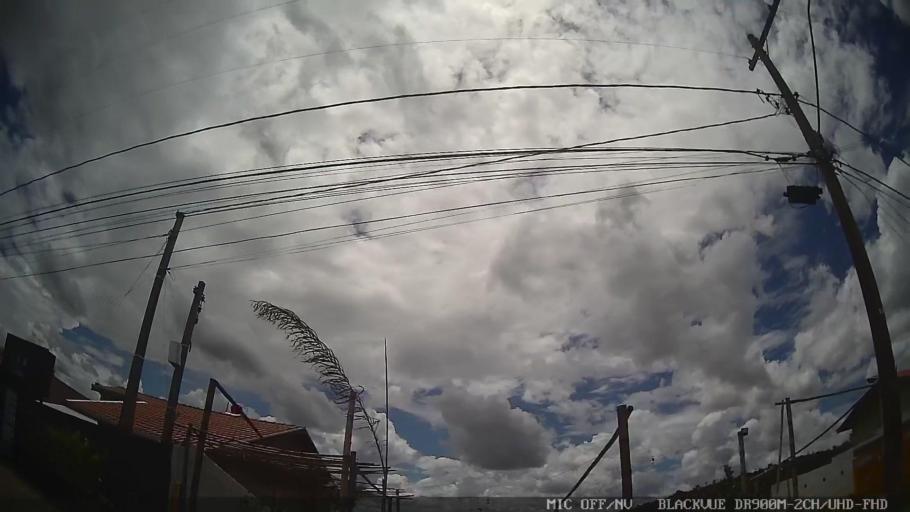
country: BR
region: Sao Paulo
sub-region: Jaguariuna
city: Jaguariuna
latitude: -22.7043
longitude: -46.9619
